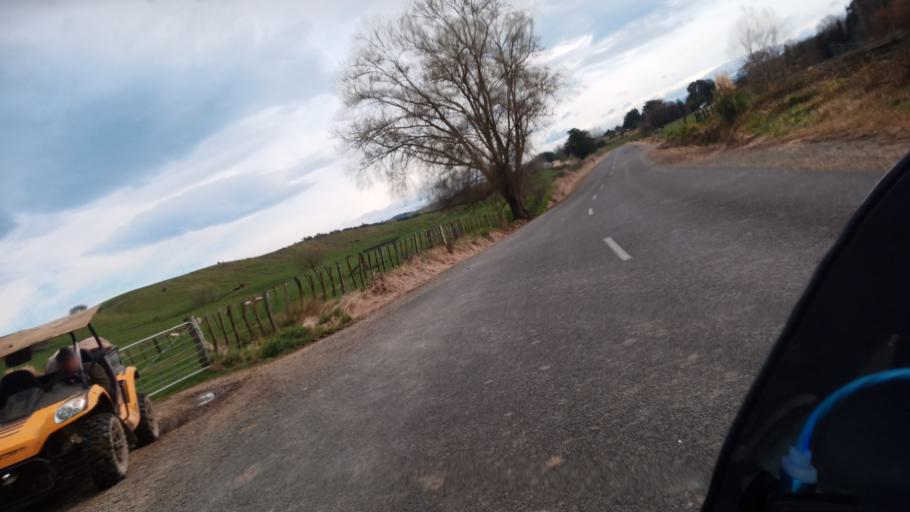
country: NZ
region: Hawke's Bay
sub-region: Wairoa District
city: Wairoa
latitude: -38.9757
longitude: 177.4228
